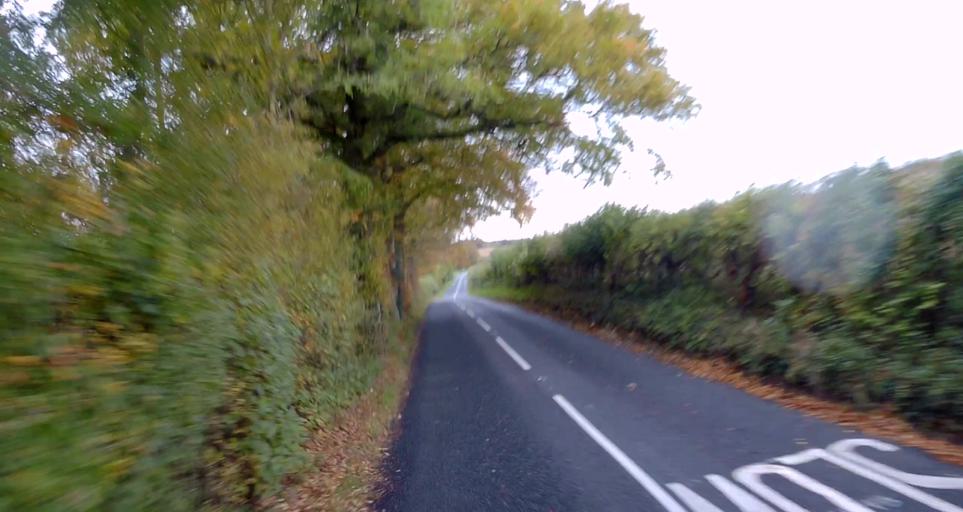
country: GB
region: England
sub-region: Hampshire
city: Four Marks
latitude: 51.1176
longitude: -1.1568
